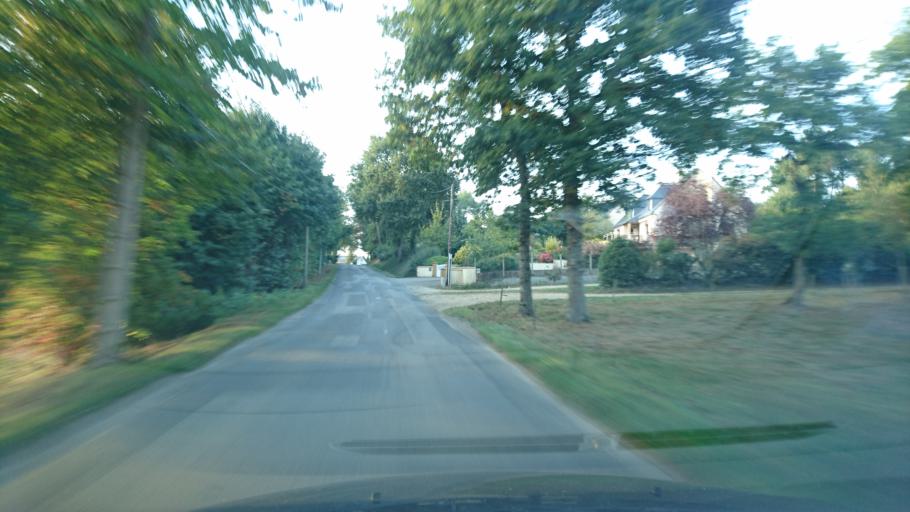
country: FR
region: Brittany
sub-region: Departement d'Ille-et-Vilaine
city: Sixt-sur-Aff
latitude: 47.7694
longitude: -2.0766
